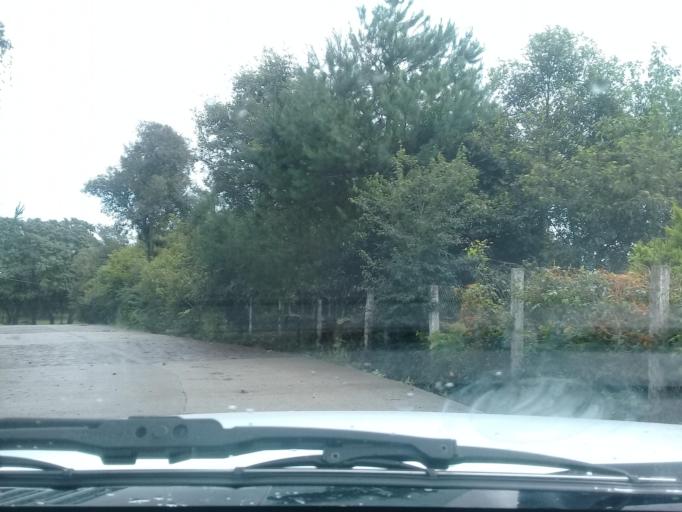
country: MX
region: Veracruz
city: Rafael Lucio
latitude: 19.5903
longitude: -96.9944
